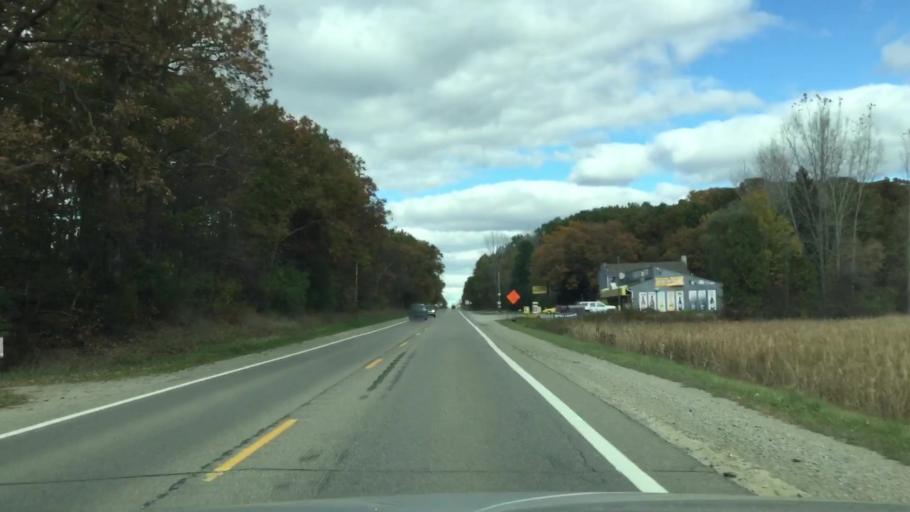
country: US
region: Michigan
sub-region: Lapeer County
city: Barnes Lake-Millers Lake
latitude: 43.1690
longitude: -83.3119
